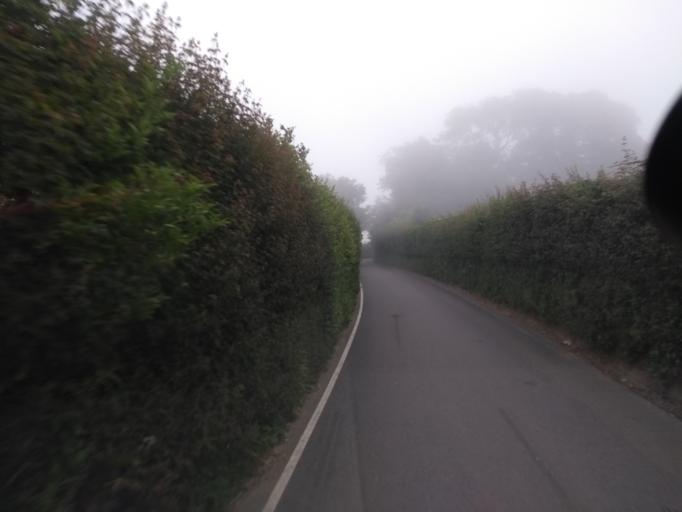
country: GB
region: England
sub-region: Dorset
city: Beaminster
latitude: 50.7813
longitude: -2.7817
